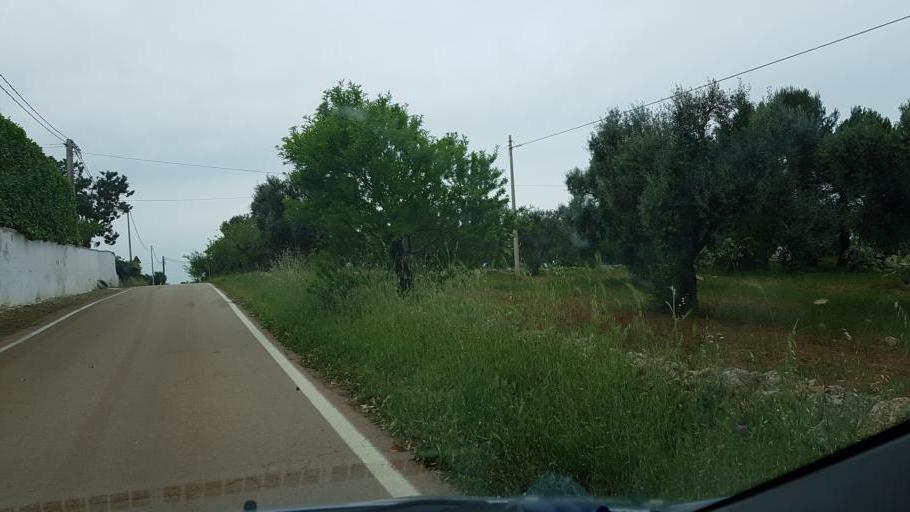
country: IT
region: Apulia
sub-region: Provincia di Brindisi
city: San Vito dei Normanni
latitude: 40.6690
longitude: 17.7583
